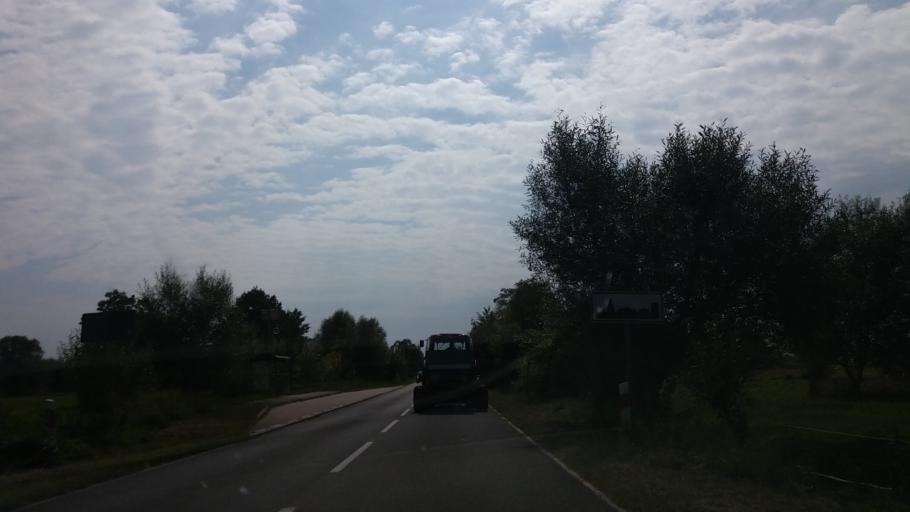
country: PL
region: Lubusz
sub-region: Powiat strzelecko-drezdenecki
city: Stare Kurowo
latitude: 52.7922
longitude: 15.6384
